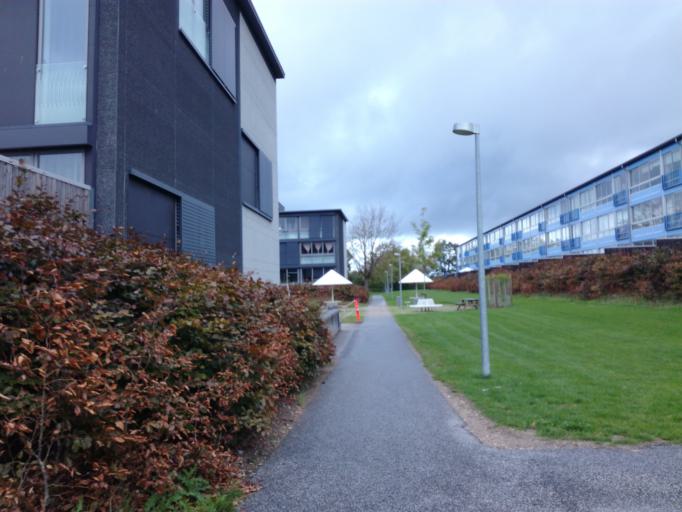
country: DK
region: South Denmark
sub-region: Fredericia Kommune
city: Fredericia
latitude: 55.5727
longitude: 9.7196
